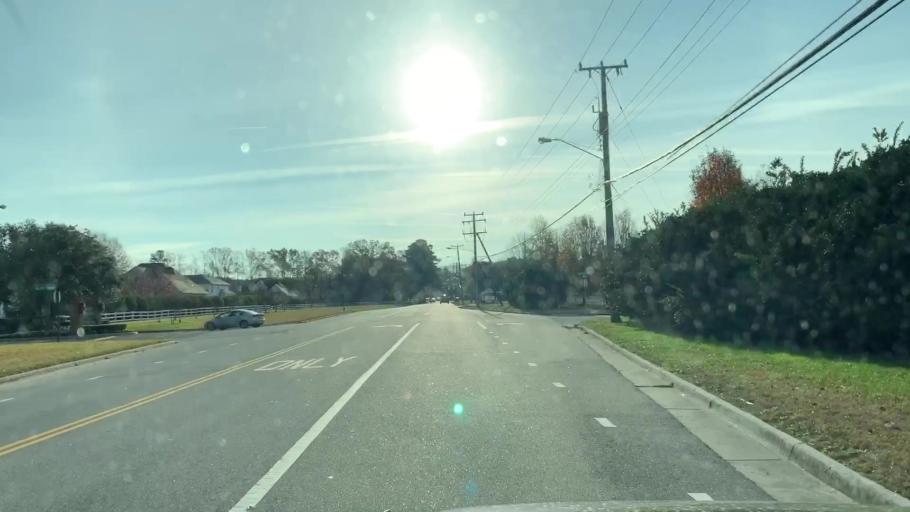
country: US
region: Virginia
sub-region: City of Chesapeake
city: Chesapeake
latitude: 36.7582
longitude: -76.1359
